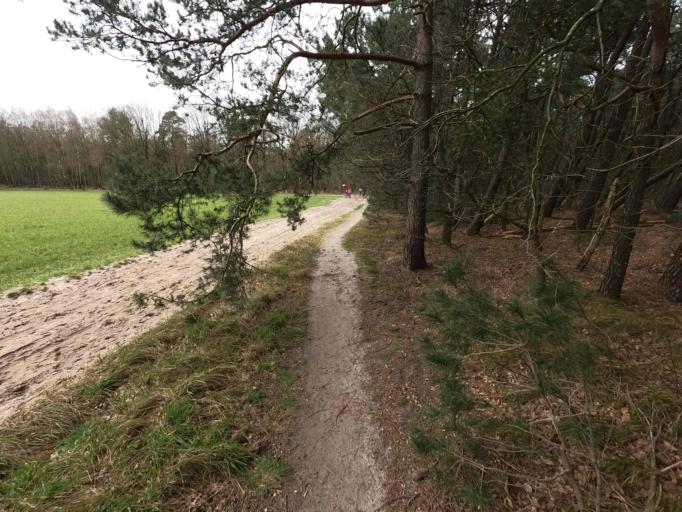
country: BE
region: Flanders
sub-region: Provincie Antwerpen
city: Kalmthout
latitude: 51.4174
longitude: 4.3986
